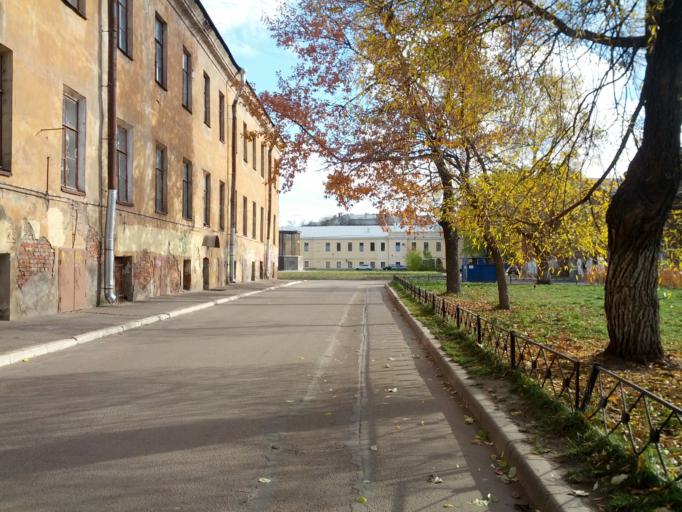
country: RU
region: St.-Petersburg
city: Saint Petersburg
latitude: 59.9242
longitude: 30.3318
